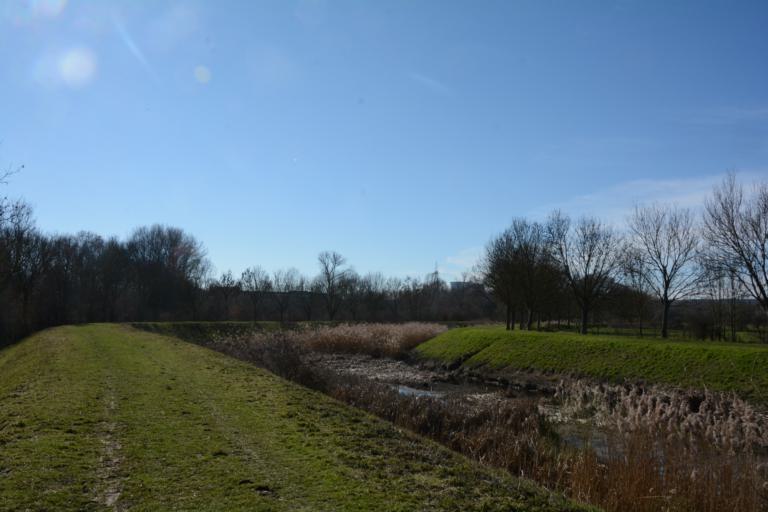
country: BE
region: Flanders
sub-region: Provincie Vlaams-Brabant
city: Vilvoorde
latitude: 50.9516
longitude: 4.4428
